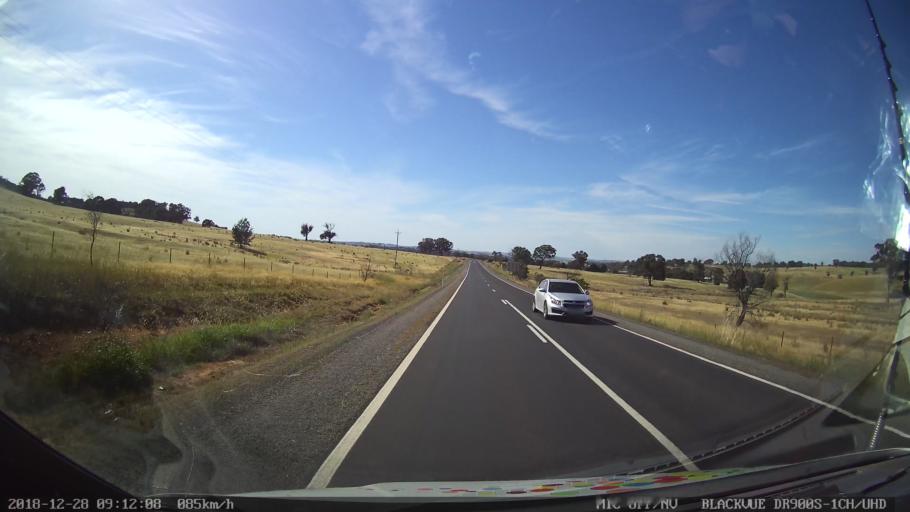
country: AU
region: New South Wales
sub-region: Upper Lachlan Shire
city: Crookwell
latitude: -34.2518
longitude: 149.3396
